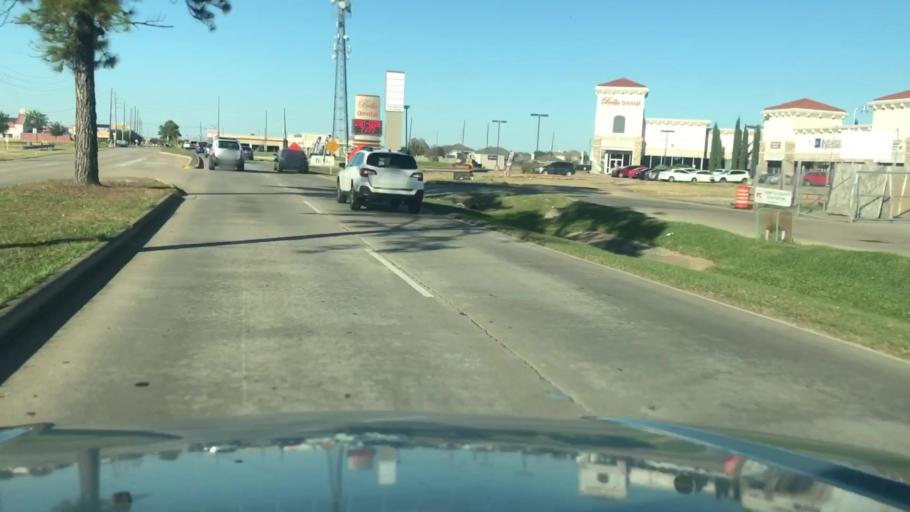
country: US
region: Texas
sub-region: Fort Bend County
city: Cinco Ranch
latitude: 29.8511
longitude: -95.7187
